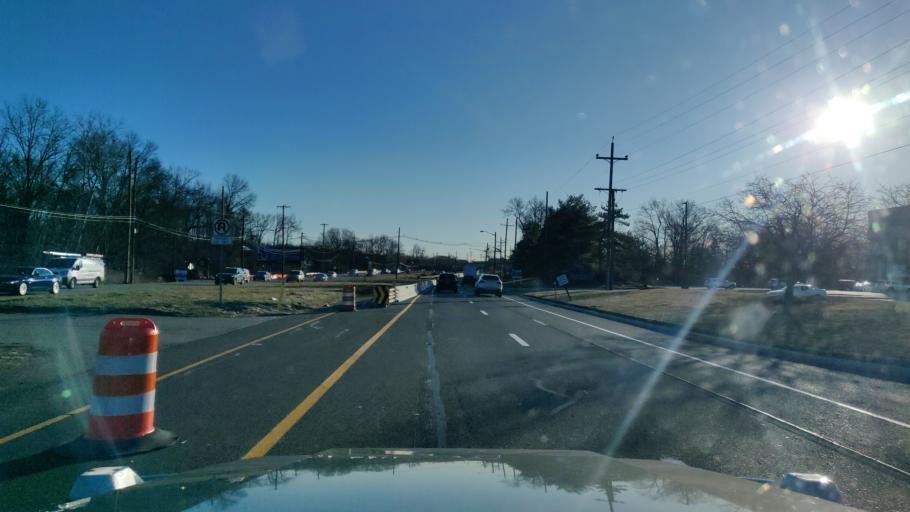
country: US
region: New Jersey
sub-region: Passaic County
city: Singac
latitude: 40.8915
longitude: -74.2688
